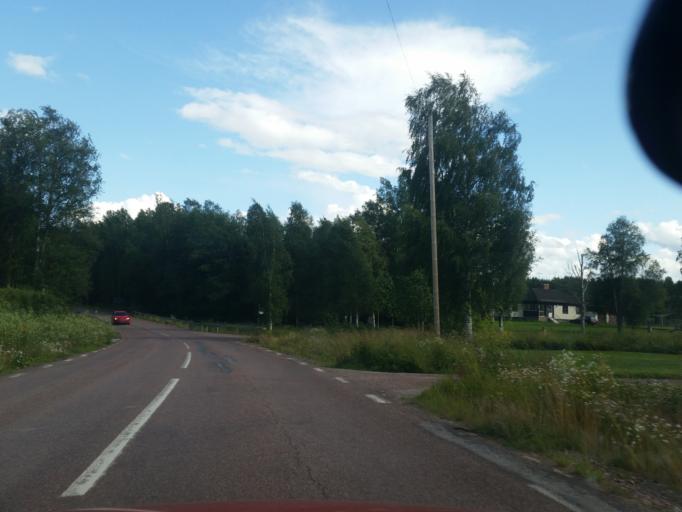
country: SE
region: Dalarna
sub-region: Gagnefs Kommun
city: Gagnef
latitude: 60.6682
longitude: 15.1534
